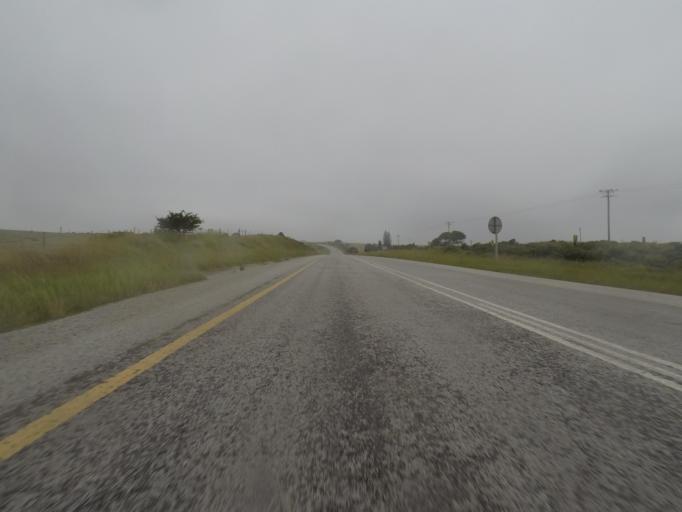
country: ZA
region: Eastern Cape
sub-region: Cacadu District Municipality
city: Grahamstown
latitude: -33.6395
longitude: 26.3261
